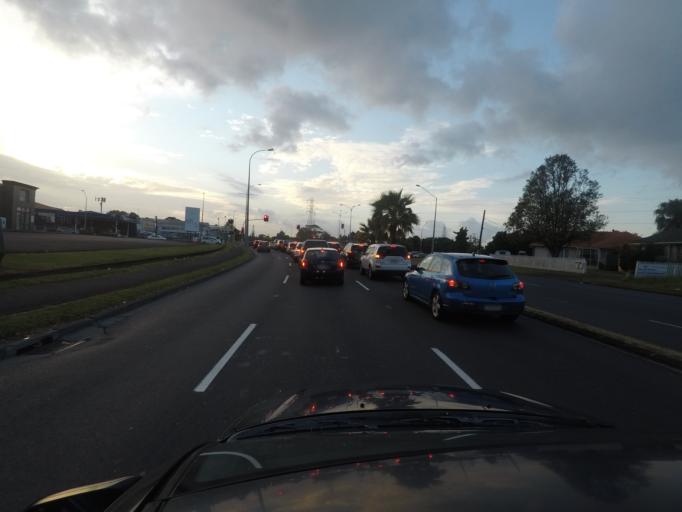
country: NZ
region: Auckland
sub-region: Auckland
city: Tamaki
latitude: -36.9143
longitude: 174.8703
